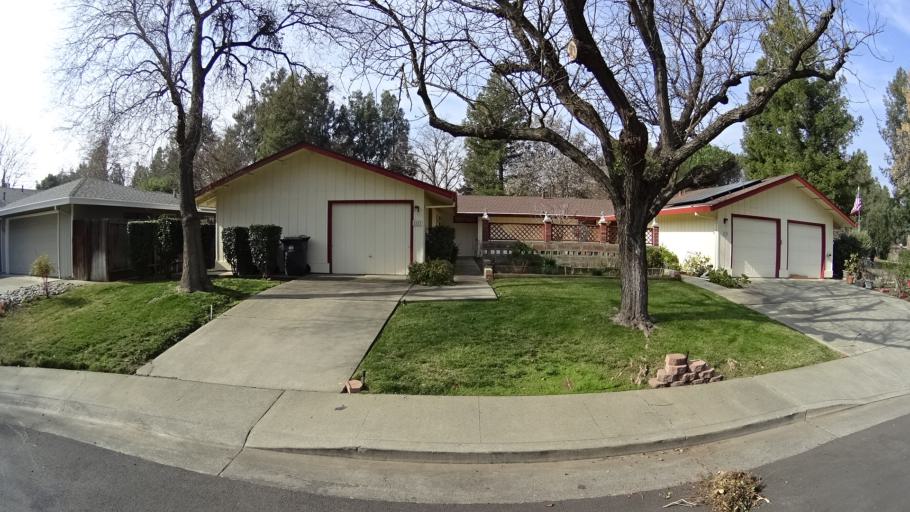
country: US
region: California
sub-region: Yolo County
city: Davis
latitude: 38.5622
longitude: -121.7544
